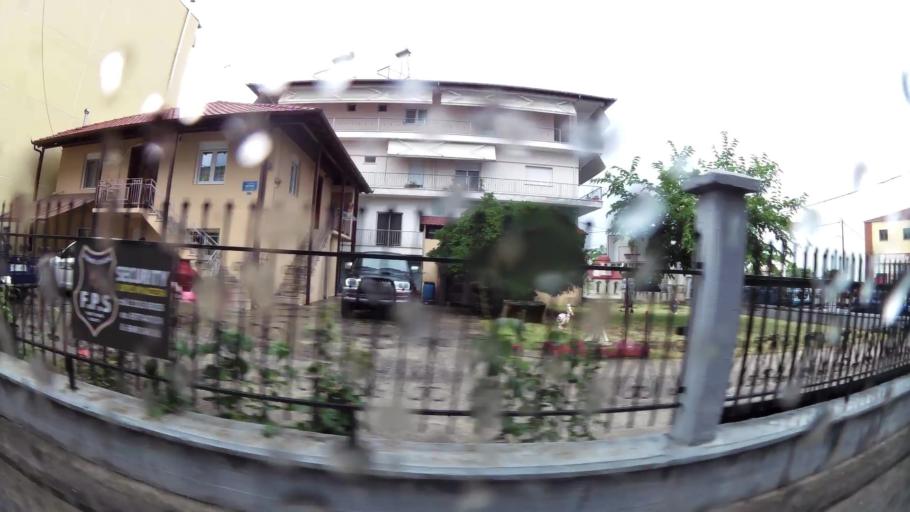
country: GR
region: Central Macedonia
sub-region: Nomos Imathias
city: Veroia
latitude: 40.5336
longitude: 22.2061
